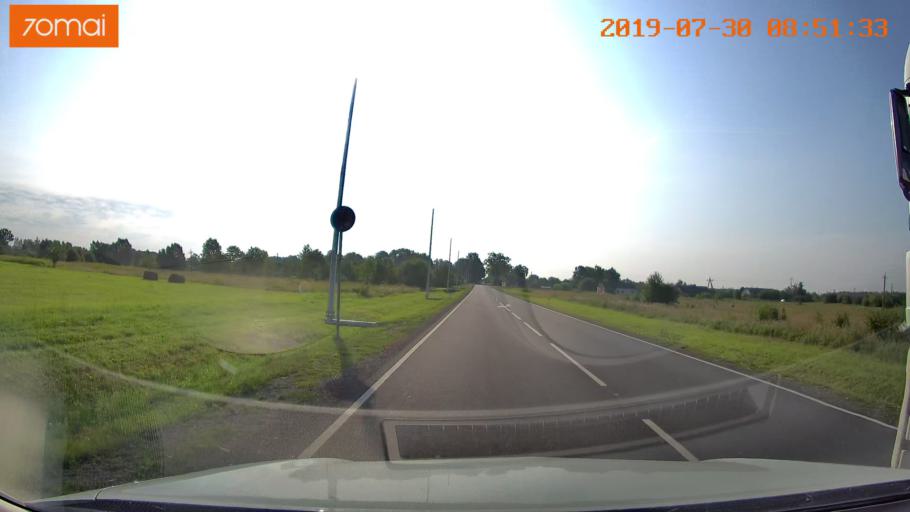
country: RU
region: Kaliningrad
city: Chernyakhovsk
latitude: 54.6021
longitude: 21.9604
